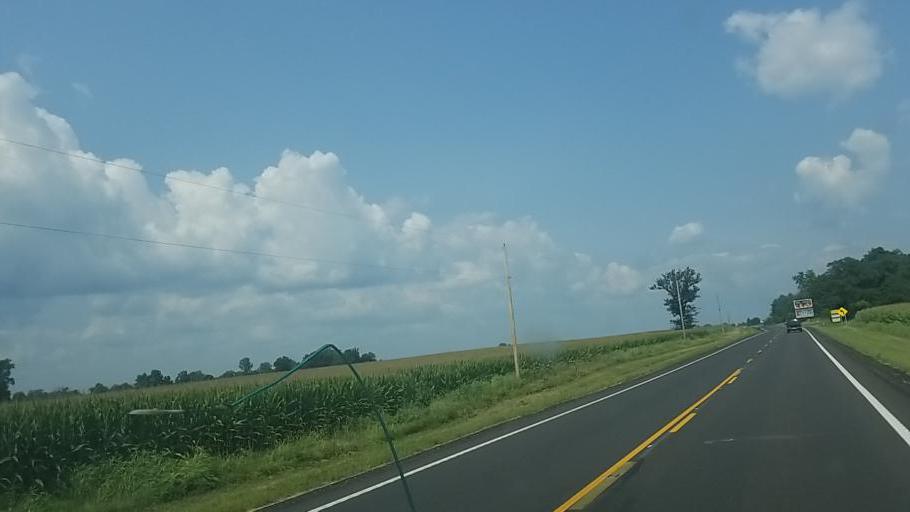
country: US
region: Ohio
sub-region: Crawford County
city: Bucyrus
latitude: 40.7598
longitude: -83.0188
